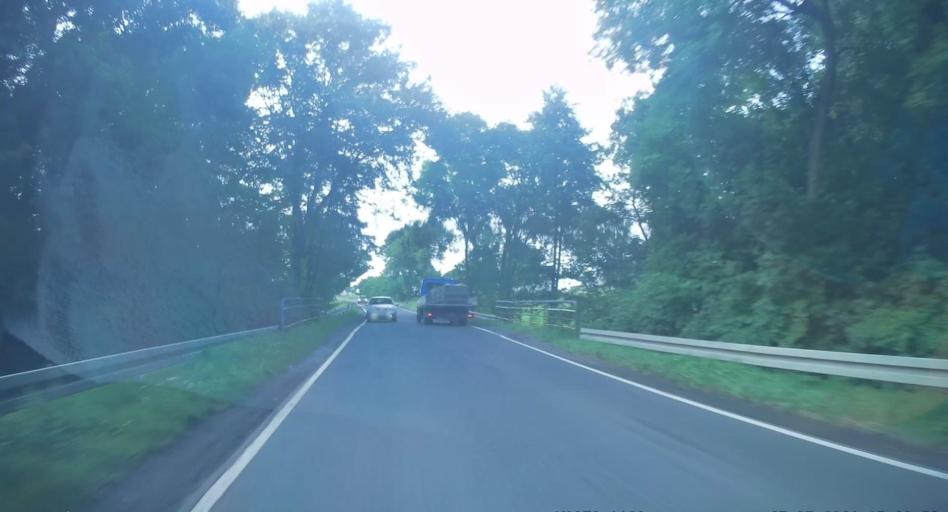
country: PL
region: Lodz Voivodeship
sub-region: Powiat tomaszowski
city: Rzeczyca
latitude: 51.6410
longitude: 20.2875
